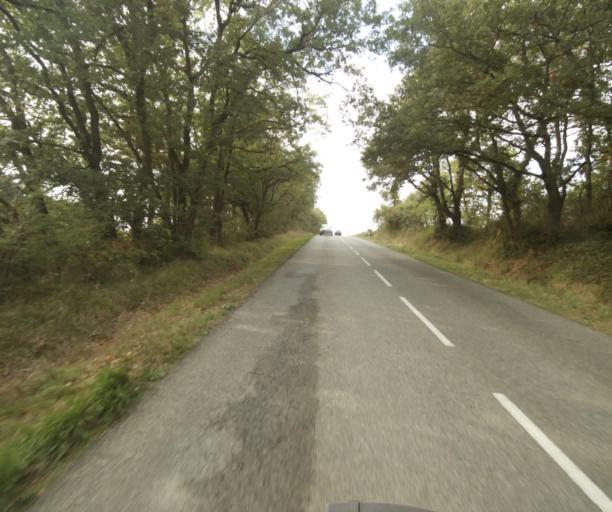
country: FR
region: Midi-Pyrenees
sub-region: Departement du Tarn-et-Garonne
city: Verdun-sur-Garonne
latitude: 43.8469
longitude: 1.1498
